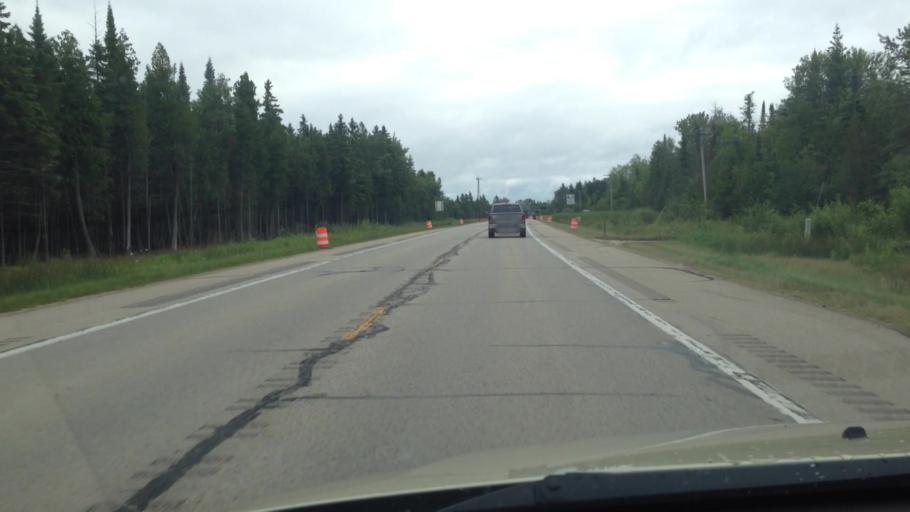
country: US
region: Michigan
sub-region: Delta County
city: Escanaba
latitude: 45.6334
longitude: -87.2025
